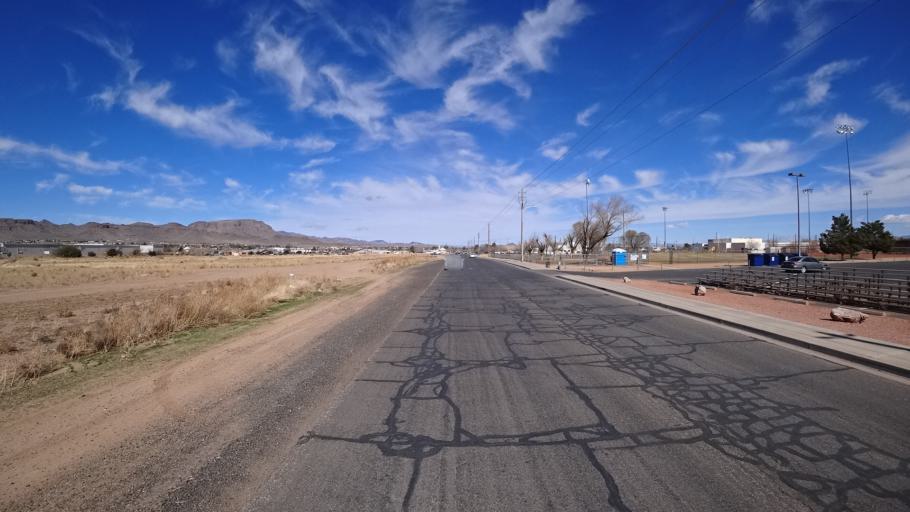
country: US
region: Arizona
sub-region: Mohave County
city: Kingman
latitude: 35.2210
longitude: -114.0292
